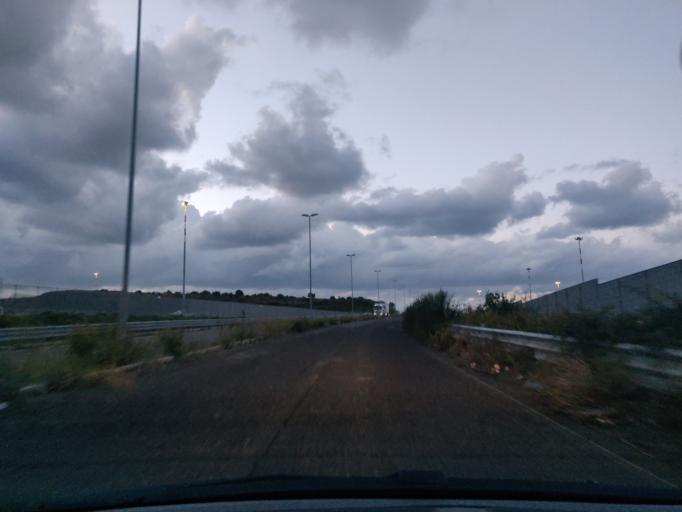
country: IT
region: Latium
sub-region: Citta metropolitana di Roma Capitale
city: Aurelia
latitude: 42.1290
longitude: 11.7780
